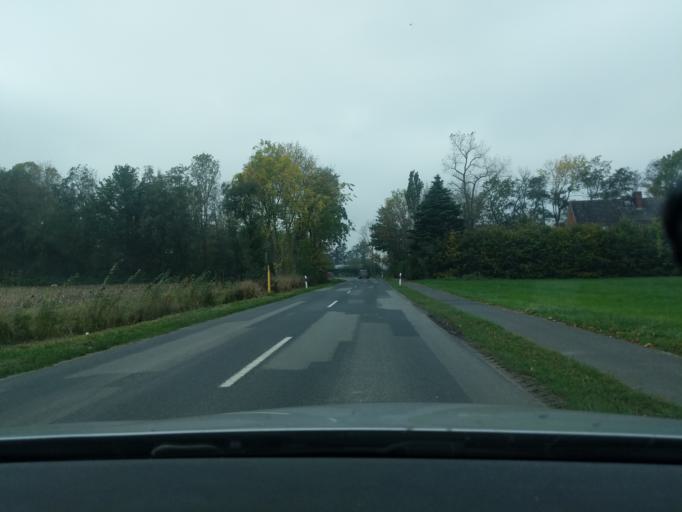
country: DE
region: Lower Saxony
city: Otterndorf
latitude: 53.8142
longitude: 8.8792
